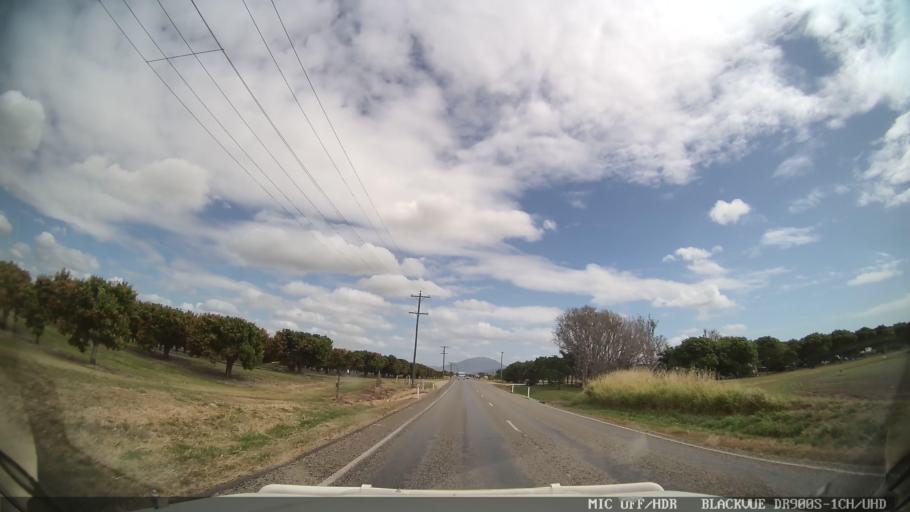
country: AU
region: Queensland
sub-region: Whitsunday
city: Bowen
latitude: -20.0155
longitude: 148.1828
